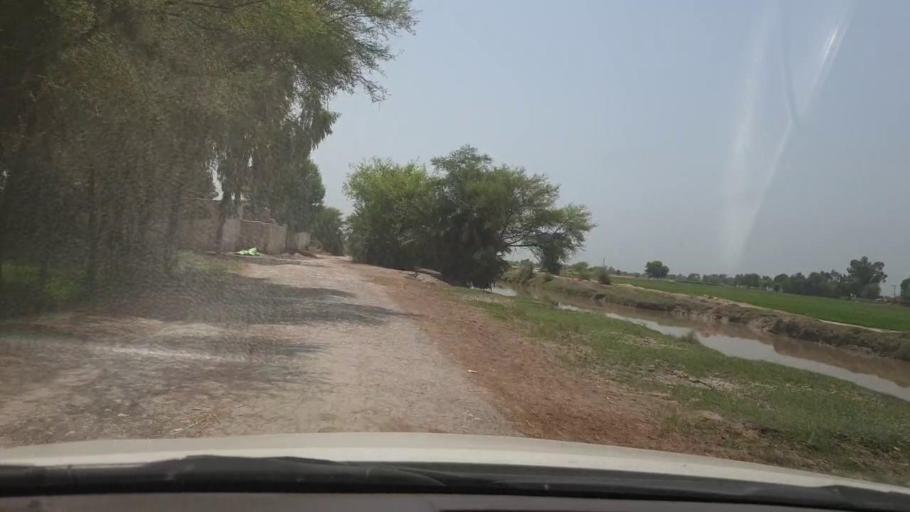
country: PK
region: Sindh
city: Shikarpur
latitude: 28.0938
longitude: 68.5767
